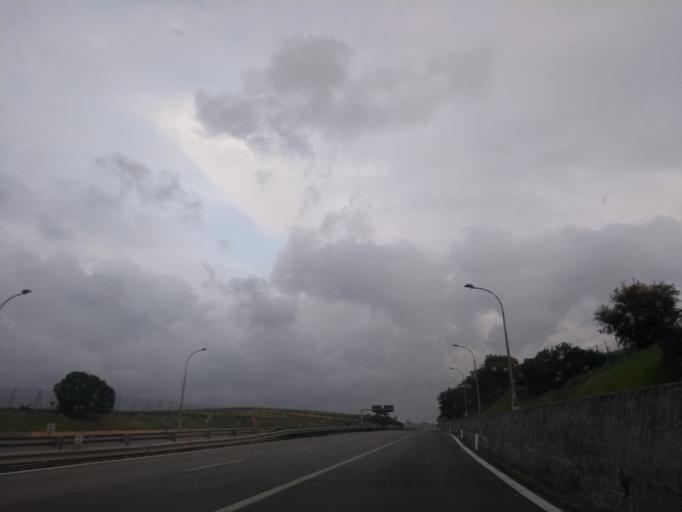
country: IT
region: Sicily
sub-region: Trapani
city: Fulgatore-Torretta
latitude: 37.9629
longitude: 12.6315
